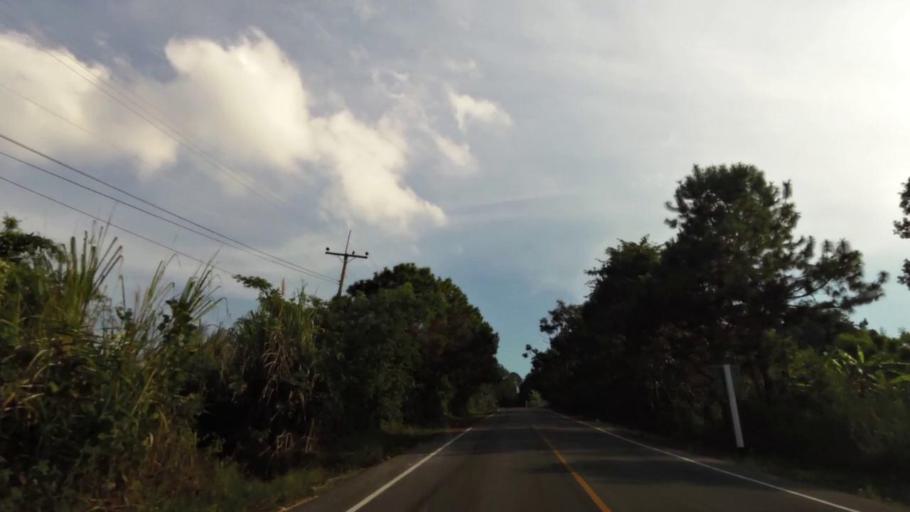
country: TH
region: Chiang Rai
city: Khun Tan
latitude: 19.8736
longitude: 100.3208
